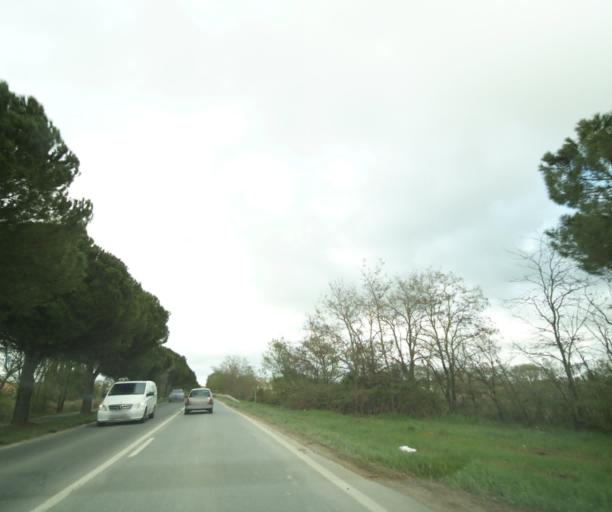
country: FR
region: Languedoc-Roussillon
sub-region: Departement de l'Herault
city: Laverune
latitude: 43.5868
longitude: 3.7942
